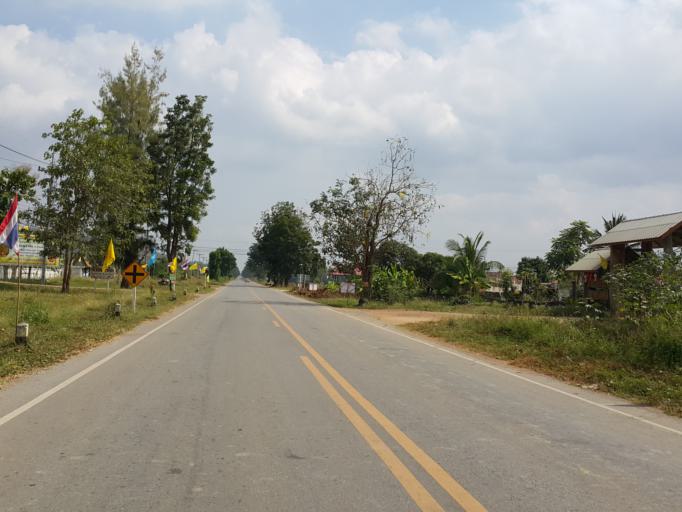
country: TH
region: Sukhothai
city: Thung Saliam
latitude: 17.3305
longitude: 99.5207
